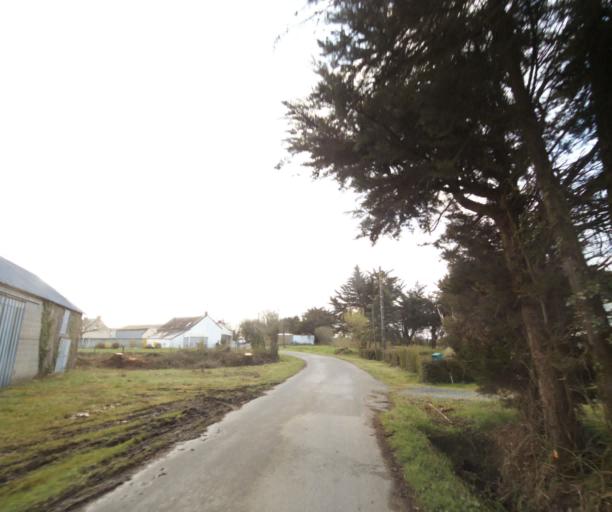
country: FR
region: Pays de la Loire
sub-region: Departement de la Loire-Atlantique
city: Savenay
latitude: 47.3873
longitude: -1.9118
